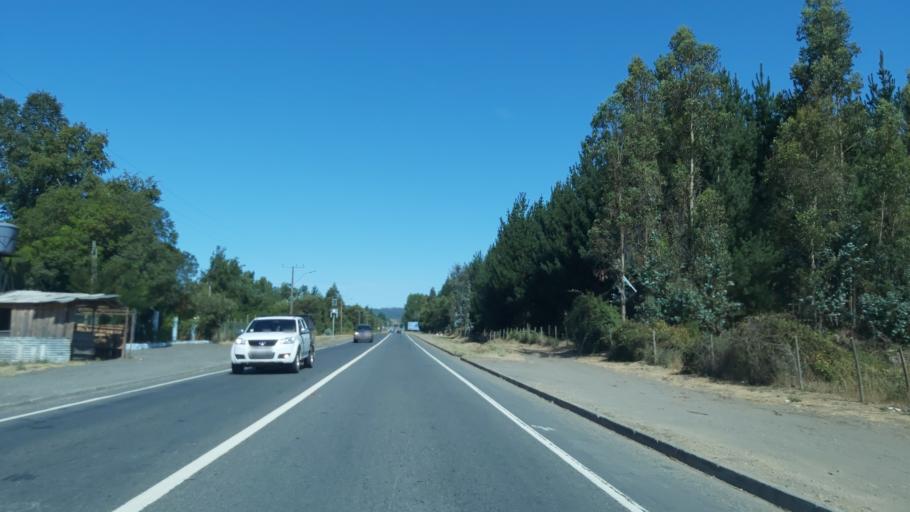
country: CL
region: Biobio
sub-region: Provincia de Concepcion
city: Lota
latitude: -37.1579
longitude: -72.9664
